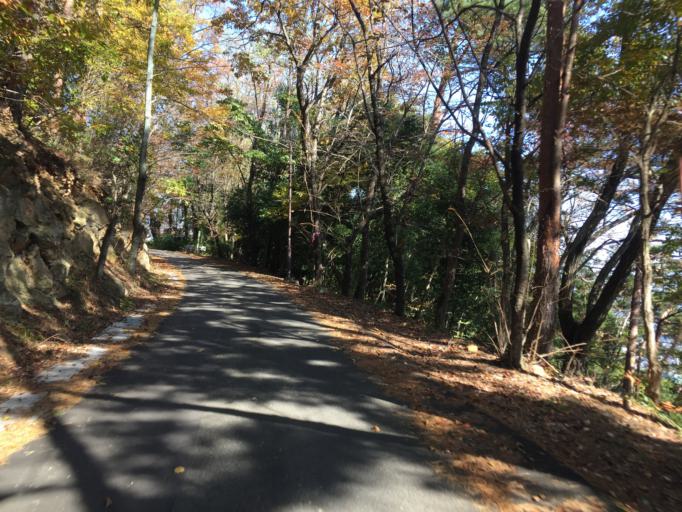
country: JP
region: Fukushima
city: Fukushima-shi
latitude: 37.7695
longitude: 140.4671
